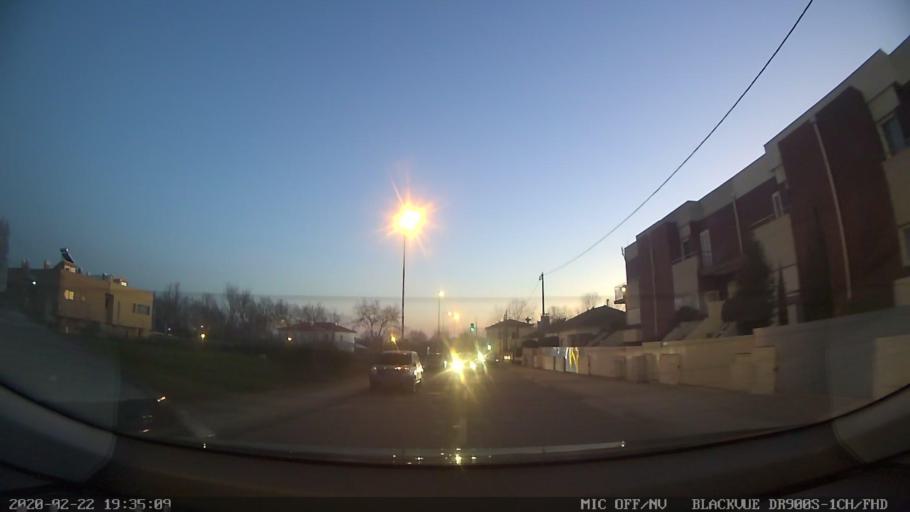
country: PT
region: Porto
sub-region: Matosinhos
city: Senhora da Hora
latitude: 41.1852
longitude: -8.6413
